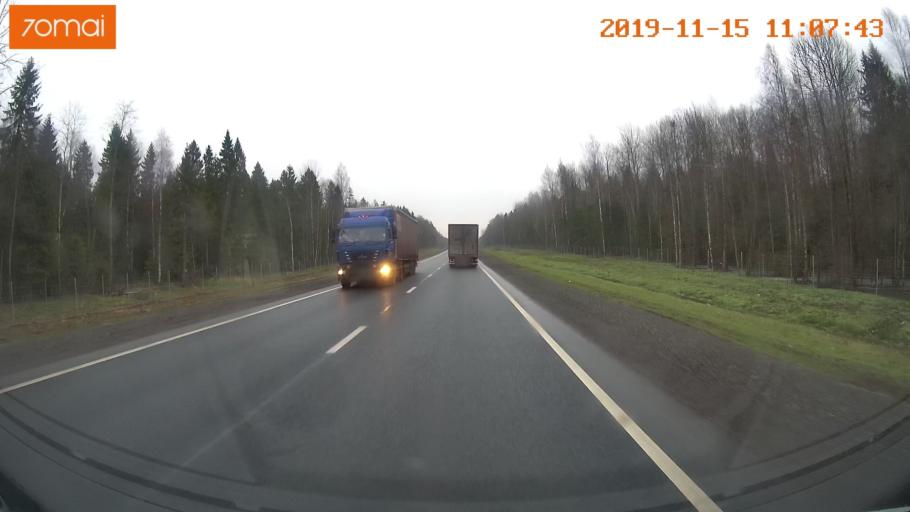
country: RU
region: Vologda
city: Chebsara
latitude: 59.1196
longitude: 39.0570
